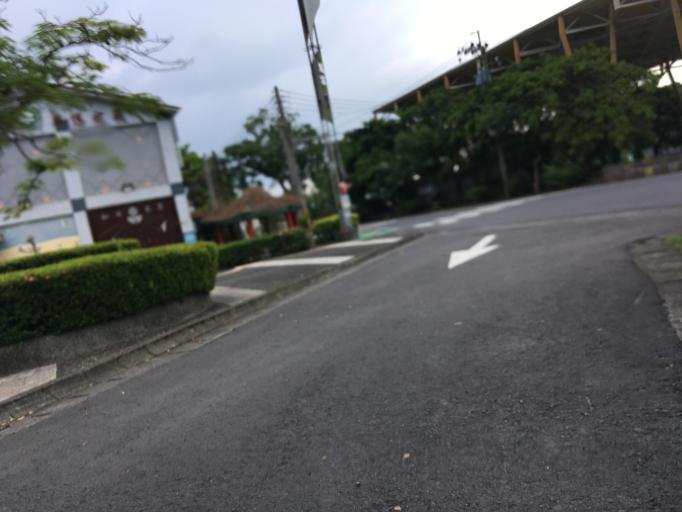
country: TW
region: Taiwan
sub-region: Yilan
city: Yilan
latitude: 24.6795
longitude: 121.6888
